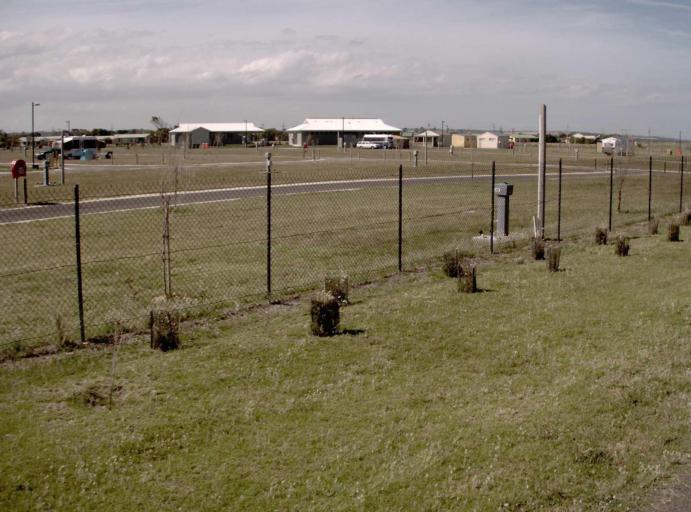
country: AU
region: Victoria
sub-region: Wellington
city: Sale
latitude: -38.3762
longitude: 147.1911
